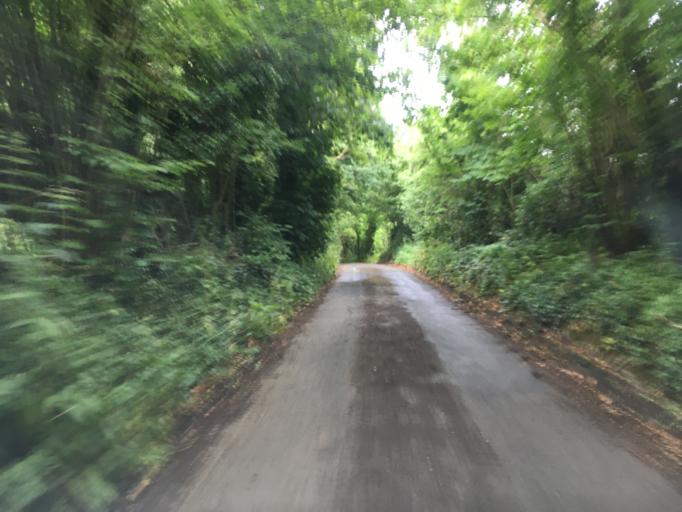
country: GB
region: England
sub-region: Gloucestershire
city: Shurdington
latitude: 51.7959
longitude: -2.0814
